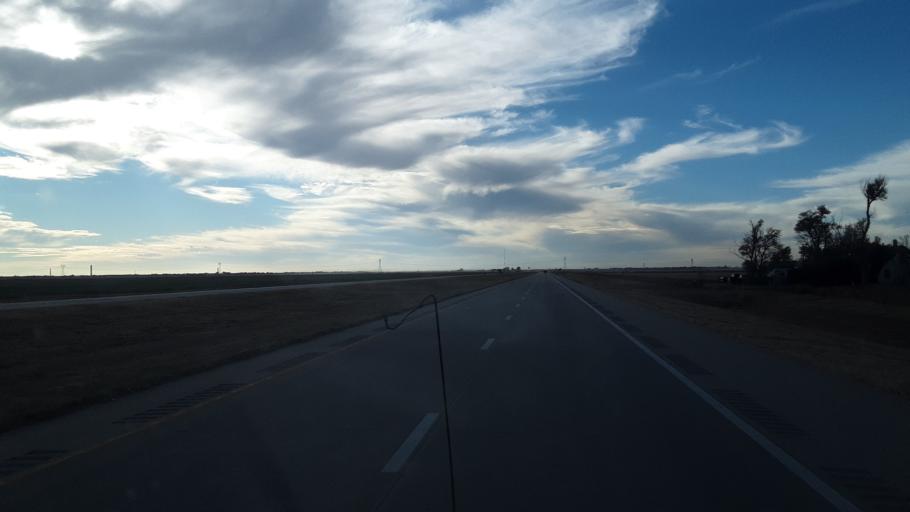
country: US
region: Kansas
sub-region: Finney County
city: Holcomb
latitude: 38.0034
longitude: -100.9470
